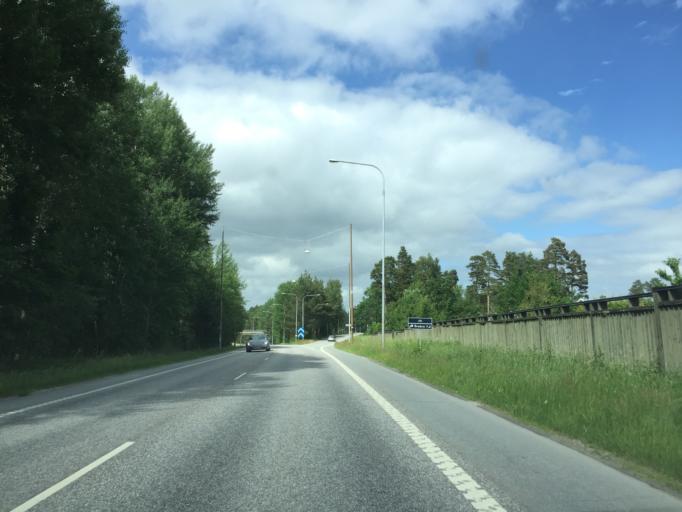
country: SE
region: OErebro
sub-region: Orebro Kommun
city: Orebro
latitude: 59.2245
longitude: 15.1473
